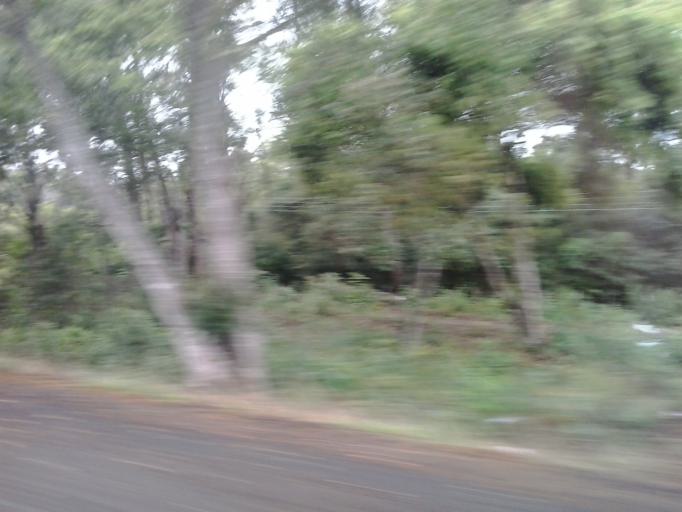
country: BR
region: Rio Grande do Sul
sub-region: Candelaria
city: Candelaria
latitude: -29.7339
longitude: -53.1775
